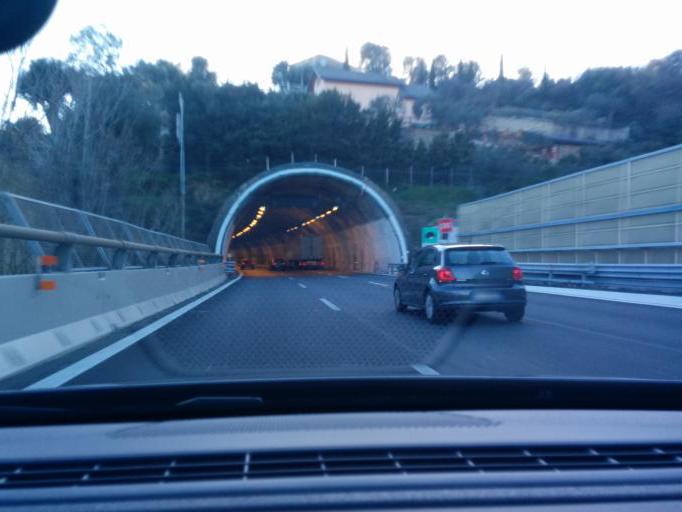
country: IT
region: Liguria
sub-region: Provincia di Genova
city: Arenzano
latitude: 44.4084
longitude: 8.6817
